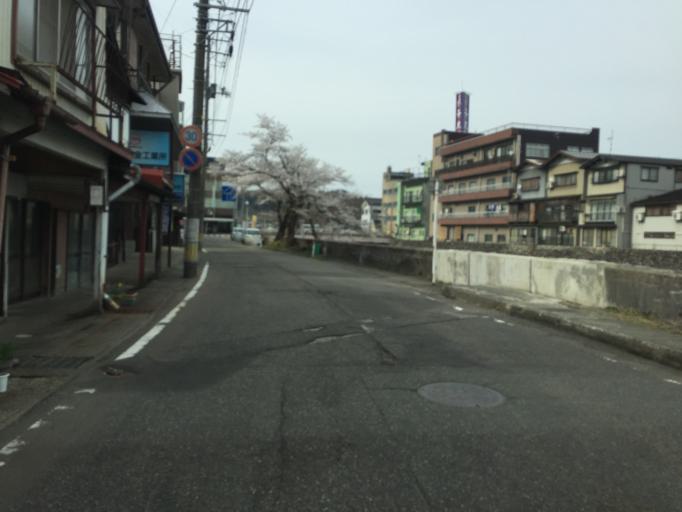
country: JP
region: Niigata
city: Tochio-honcho
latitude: 37.4749
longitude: 138.9940
